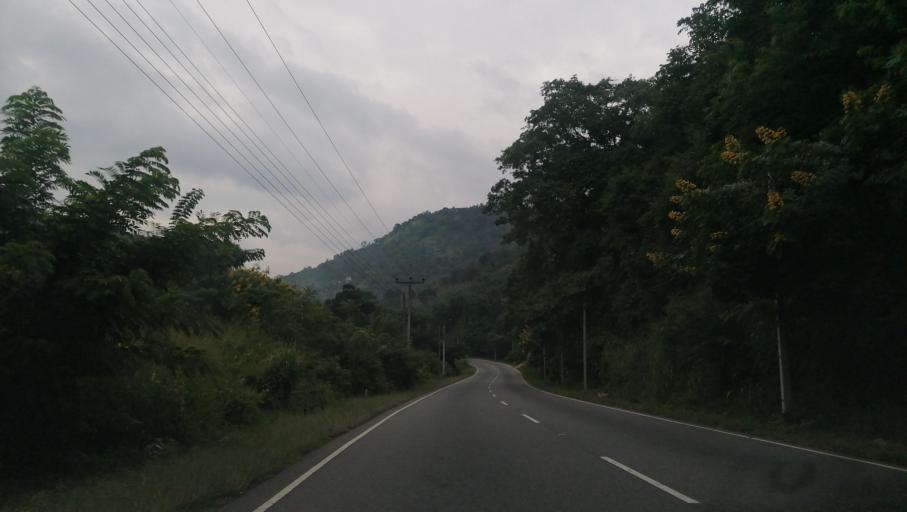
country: LK
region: Central
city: Kandy
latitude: 7.2461
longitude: 80.7267
